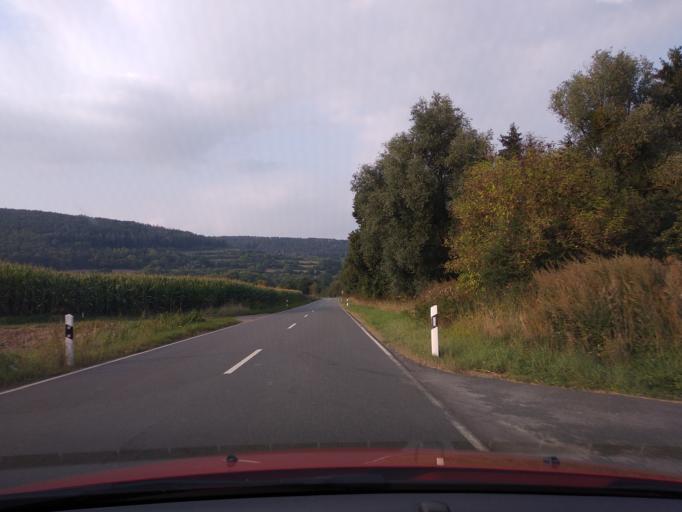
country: DE
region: North Rhine-Westphalia
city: Beverungen
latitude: 51.6527
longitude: 9.3515
